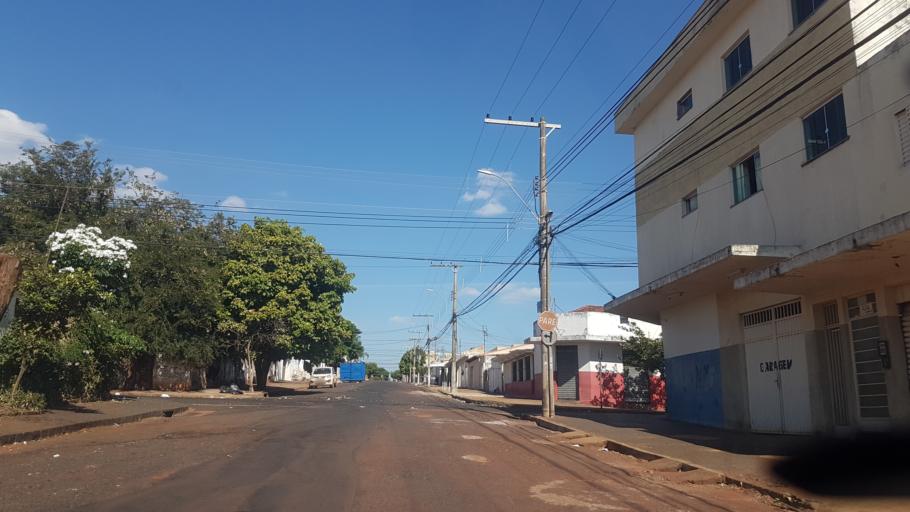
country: BR
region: Minas Gerais
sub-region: Uberlandia
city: Uberlandia
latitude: -18.9074
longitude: -48.2894
